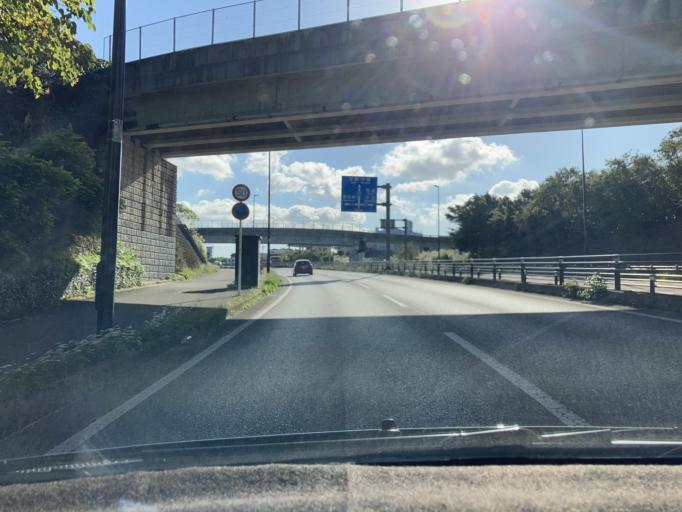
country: JP
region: Okinawa
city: Ishikawa
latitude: 26.4225
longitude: 127.8154
